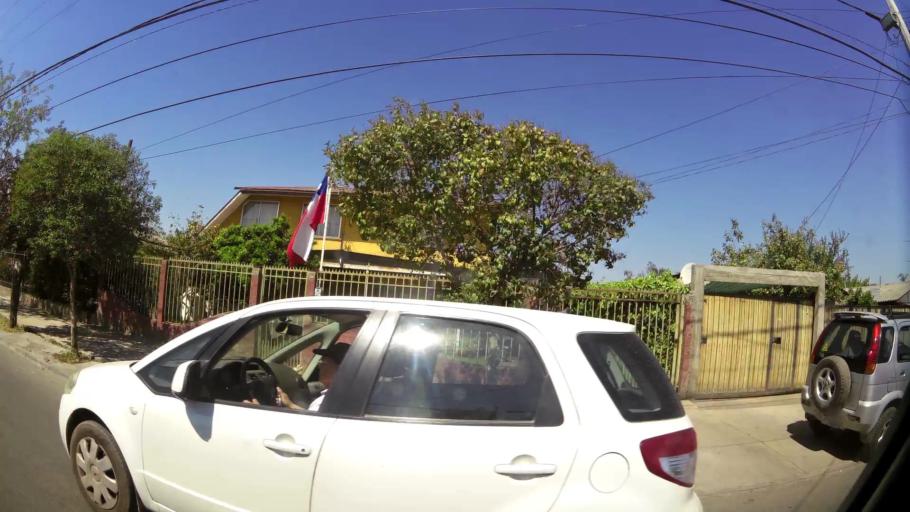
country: CL
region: Santiago Metropolitan
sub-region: Provincia de Talagante
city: Penaflor
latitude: -33.5689
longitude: -70.8092
